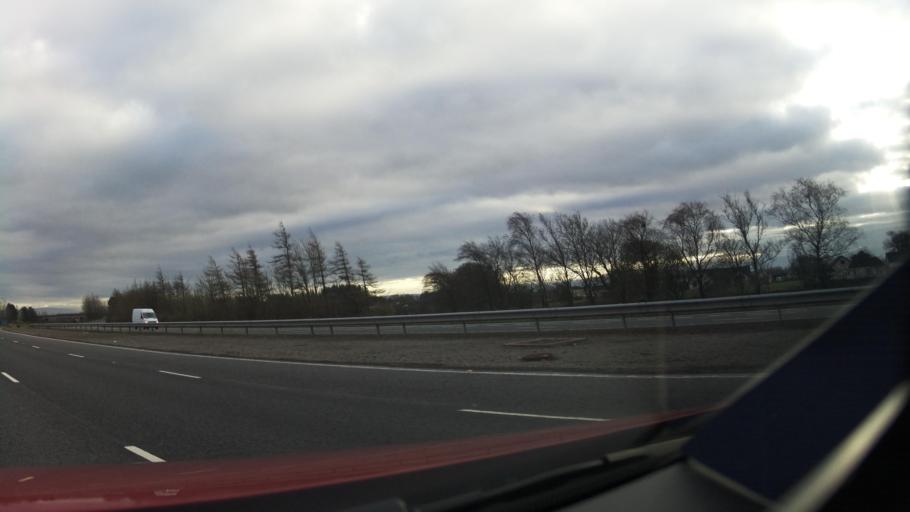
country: GB
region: Scotland
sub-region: Dumfries and Galloway
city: Gretna
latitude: 55.0278
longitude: -3.1350
